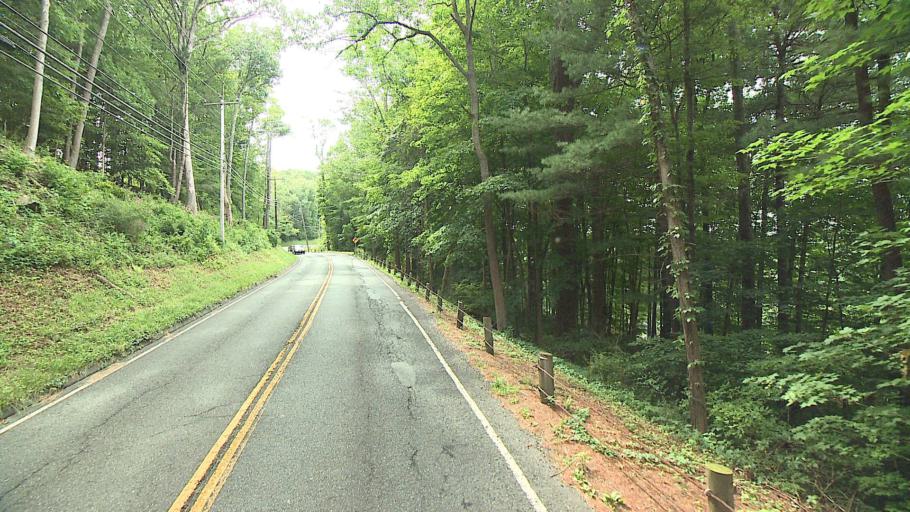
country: US
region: Connecticut
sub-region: Litchfield County
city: New Preston
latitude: 41.6376
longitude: -73.3170
